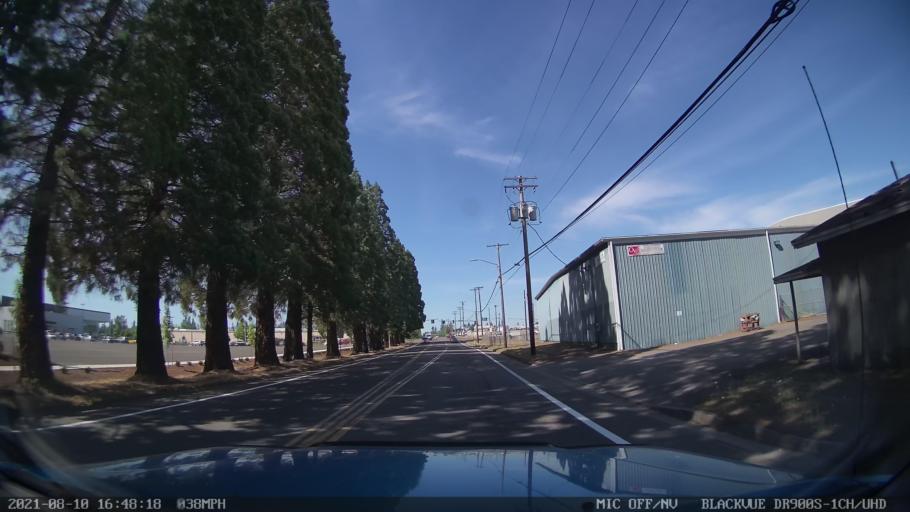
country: US
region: Oregon
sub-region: Marion County
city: Keizer
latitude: 44.9682
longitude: -123.0198
